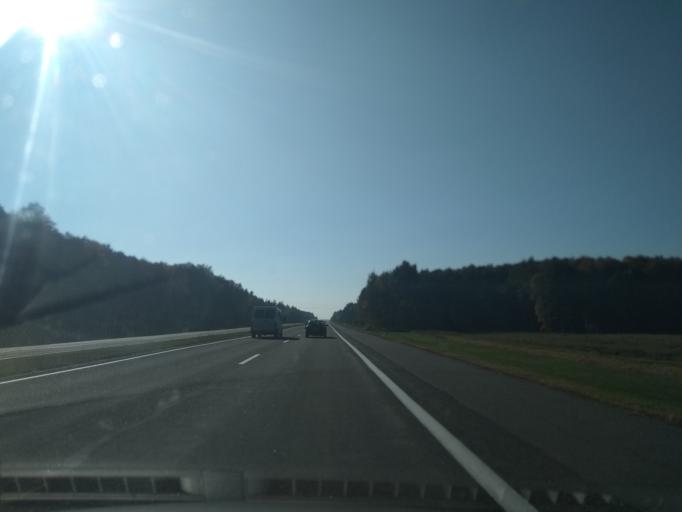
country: BY
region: Brest
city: Ivatsevichy
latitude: 52.8087
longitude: 25.5755
